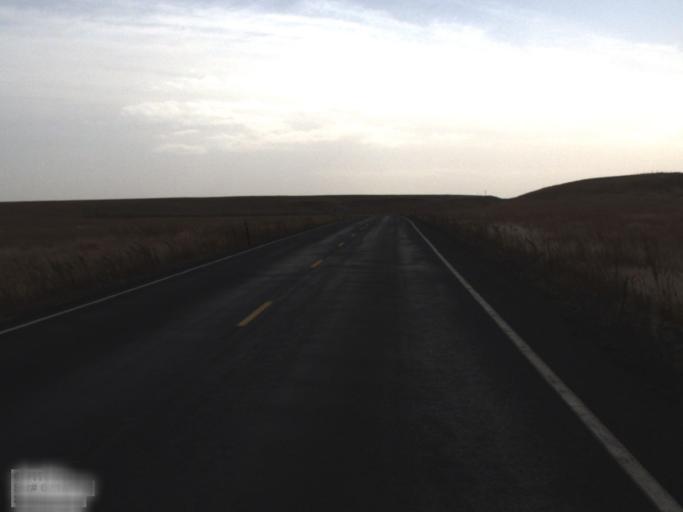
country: US
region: Washington
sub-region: Adams County
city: Ritzville
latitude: 47.4018
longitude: -118.6855
